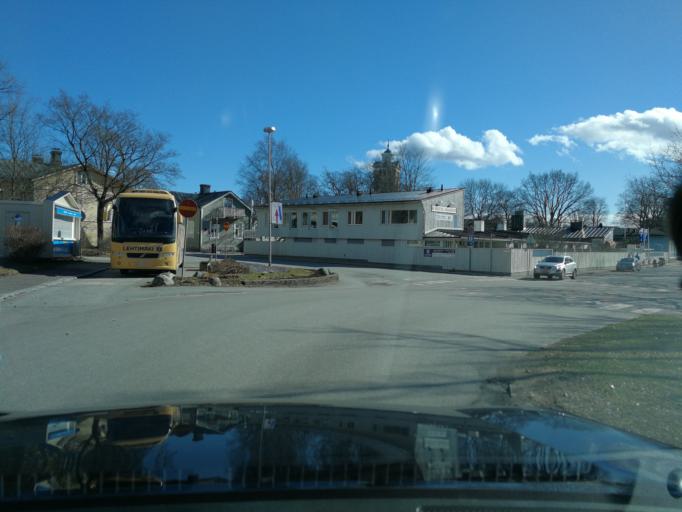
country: FI
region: Uusimaa
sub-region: Raaseporin
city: Ekenaes
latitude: 59.9758
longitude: 23.4330
